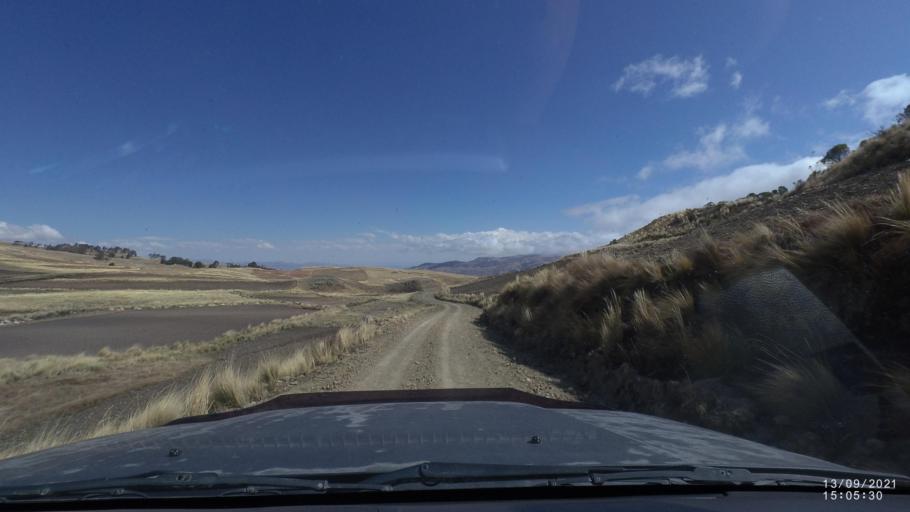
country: BO
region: Cochabamba
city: Colomi
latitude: -17.3439
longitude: -65.7918
